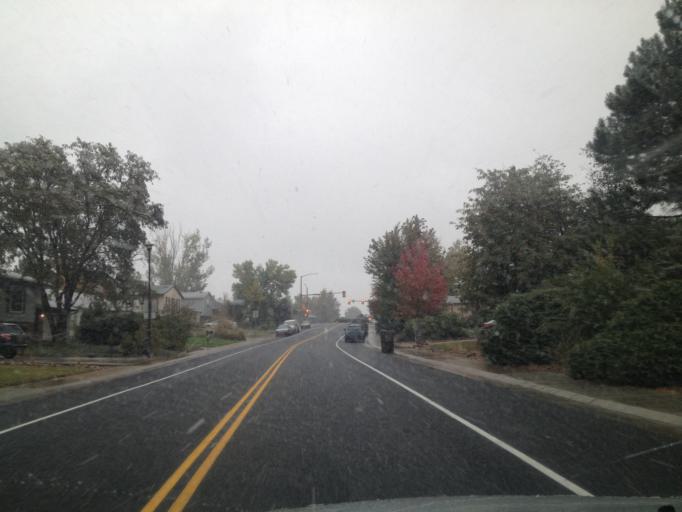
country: US
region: Colorado
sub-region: Boulder County
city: Louisville
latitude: 39.9855
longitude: -105.1544
